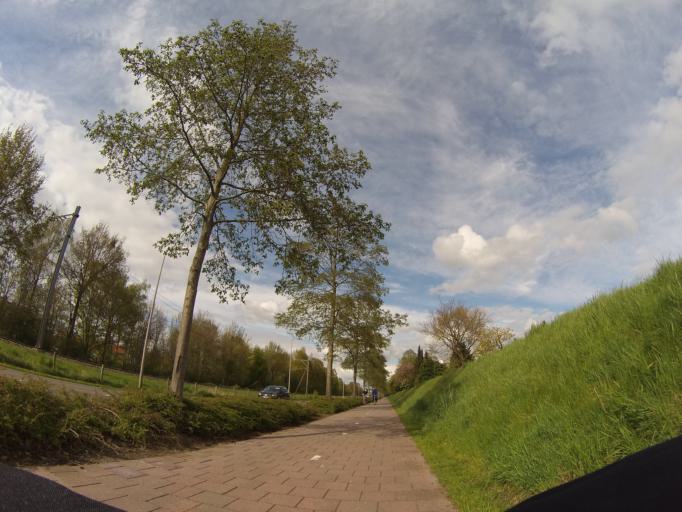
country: NL
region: Drenthe
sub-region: Gemeente Coevorden
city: Coevorden
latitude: 52.6694
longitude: 6.7394
